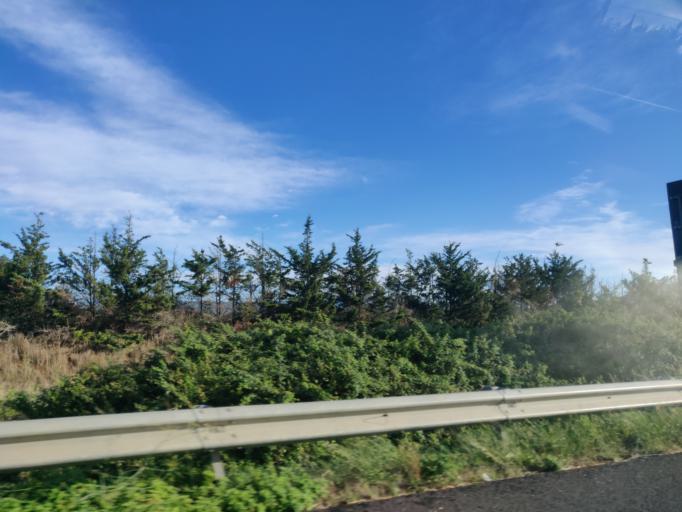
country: IT
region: Tuscany
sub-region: Provincia di Grosseto
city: Grosseto
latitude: 42.7961
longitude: 11.1135
